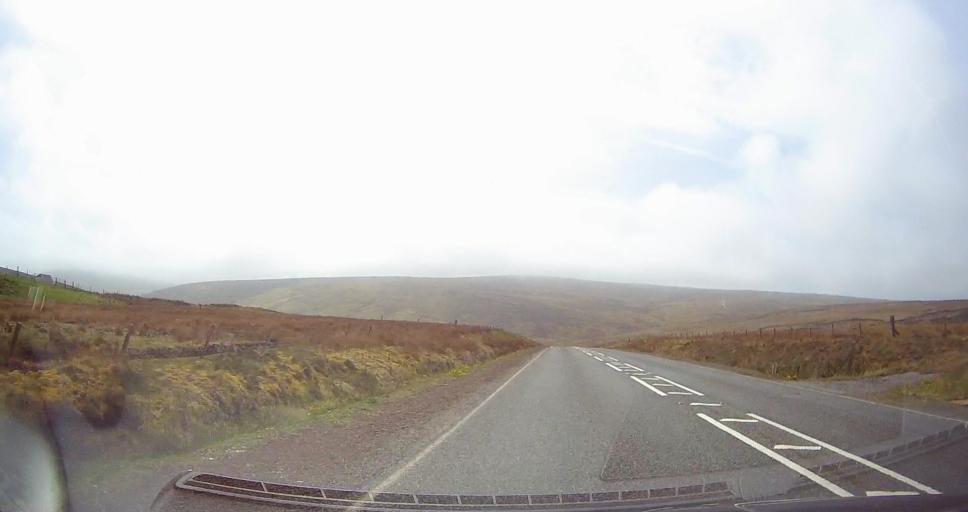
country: GB
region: Scotland
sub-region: Shetland Islands
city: Sandwick
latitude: 60.0084
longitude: -1.2693
